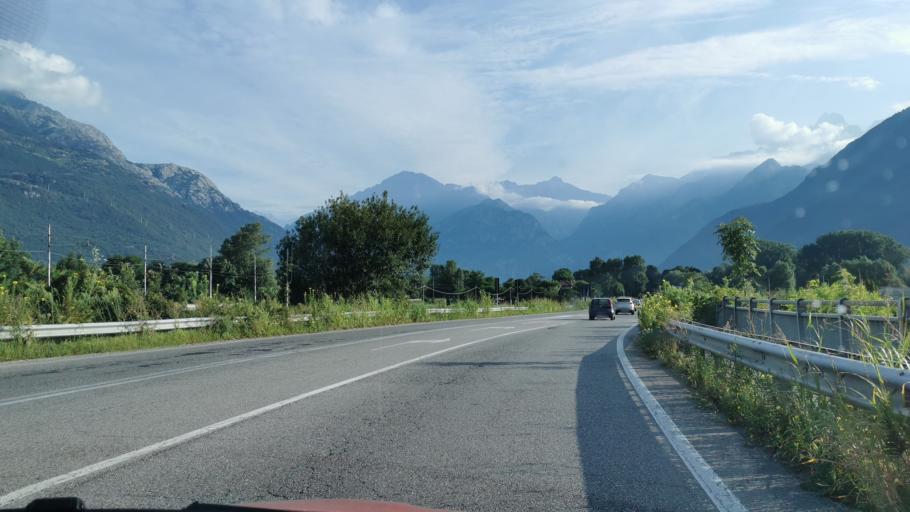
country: IT
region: Lombardy
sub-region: Provincia di Sondrio
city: Piantedo
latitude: 46.1509
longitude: 9.4126
